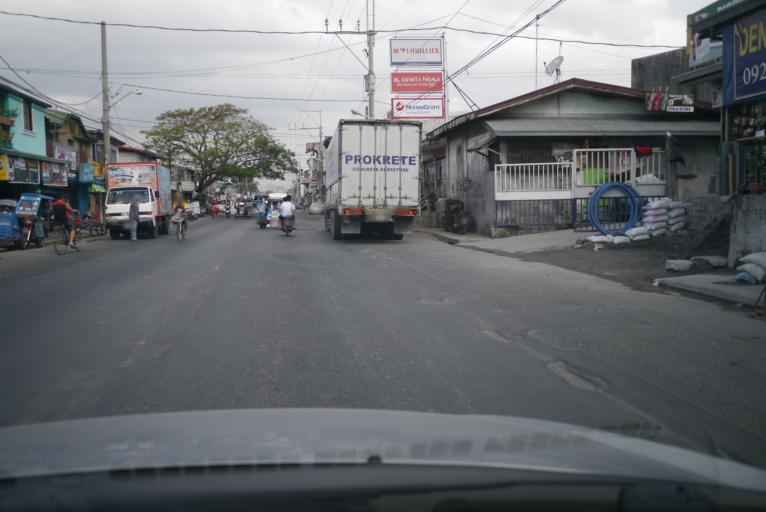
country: PH
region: Calabarzon
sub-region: Province of Rizal
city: Cainta
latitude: 14.5703
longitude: 121.1058
